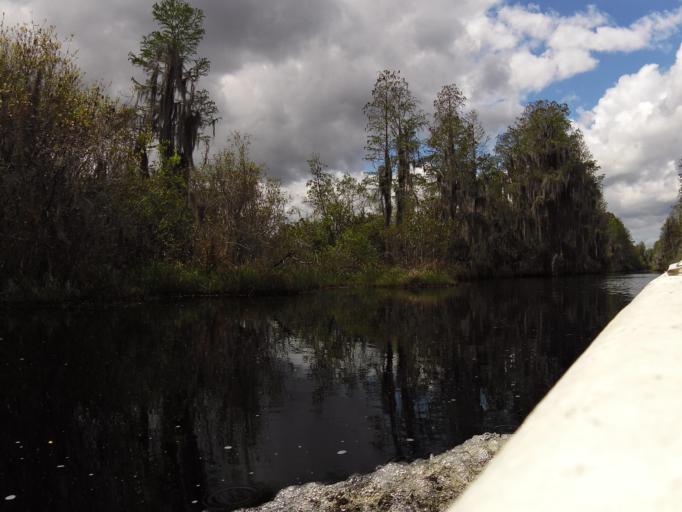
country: US
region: Georgia
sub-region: Charlton County
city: Folkston
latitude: 30.7370
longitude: -82.1682
